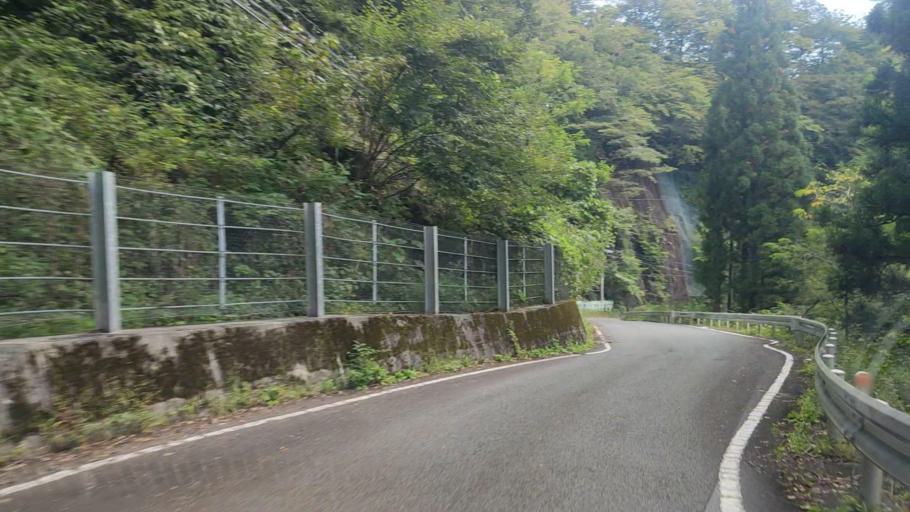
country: JP
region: Gunma
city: Nakanojomachi
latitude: 36.6499
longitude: 138.6409
